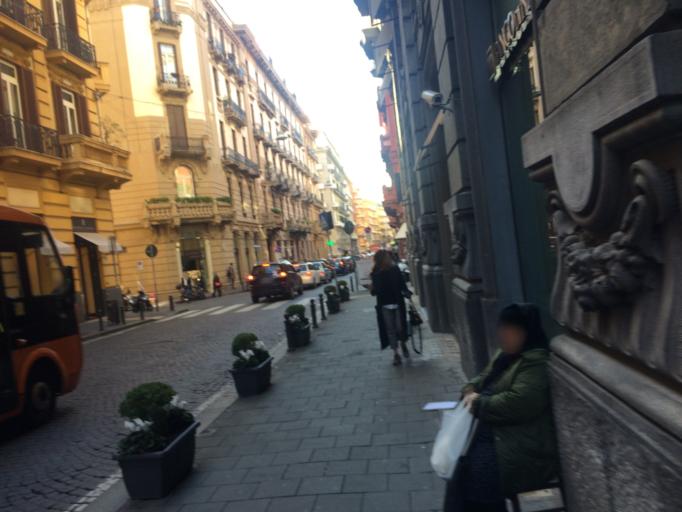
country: IT
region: Campania
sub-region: Provincia di Napoli
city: Napoli
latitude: 40.8366
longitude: 14.2396
